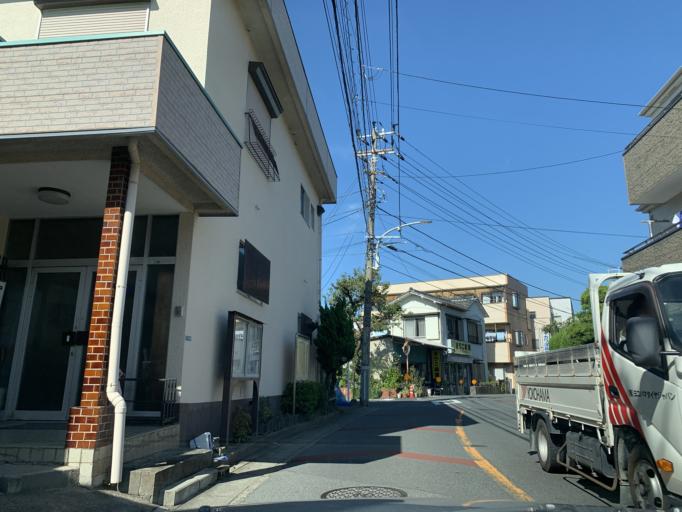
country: JP
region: Tokyo
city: Urayasu
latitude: 35.6753
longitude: 139.8920
